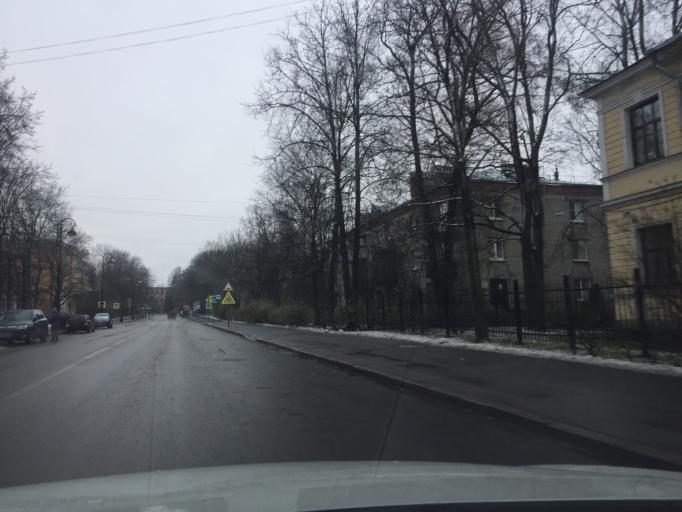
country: RU
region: St.-Petersburg
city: Pushkin
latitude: 59.7226
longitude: 30.4039
